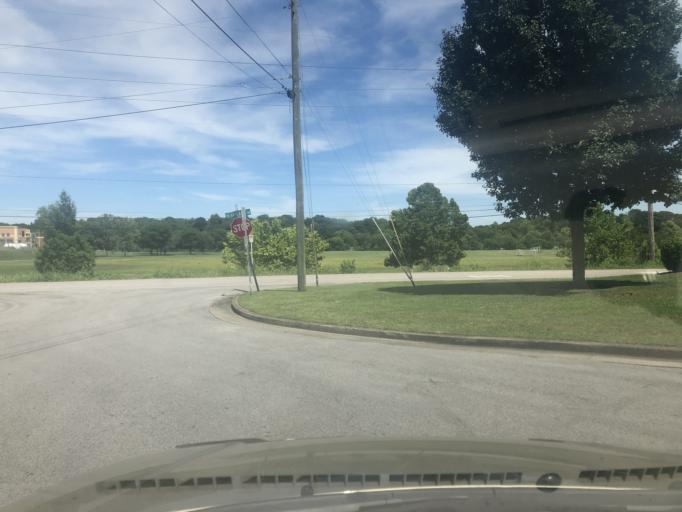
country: US
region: Tennessee
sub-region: Davidson County
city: Lakewood
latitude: 36.1893
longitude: -86.6690
